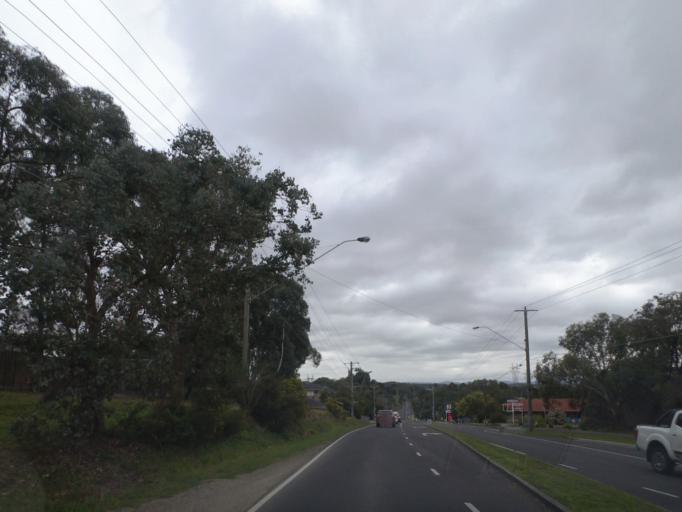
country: AU
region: Victoria
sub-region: Nillumbik
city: Eltham North
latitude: -37.6888
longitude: 145.1425
